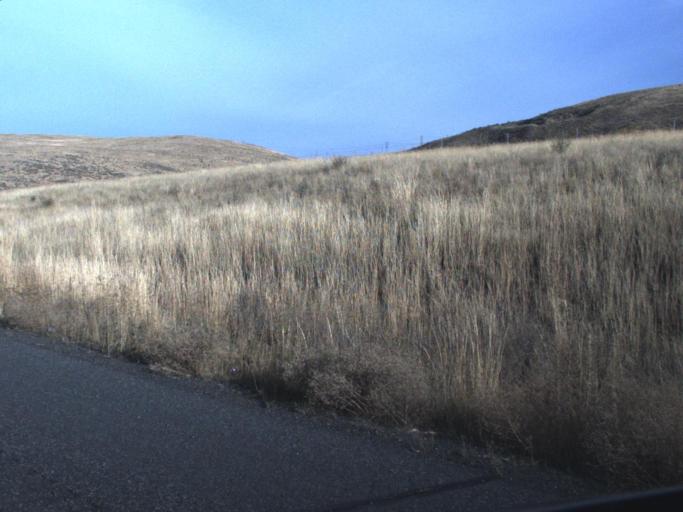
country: US
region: Oregon
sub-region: Umatilla County
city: Umatilla
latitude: 45.9860
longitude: -119.3058
